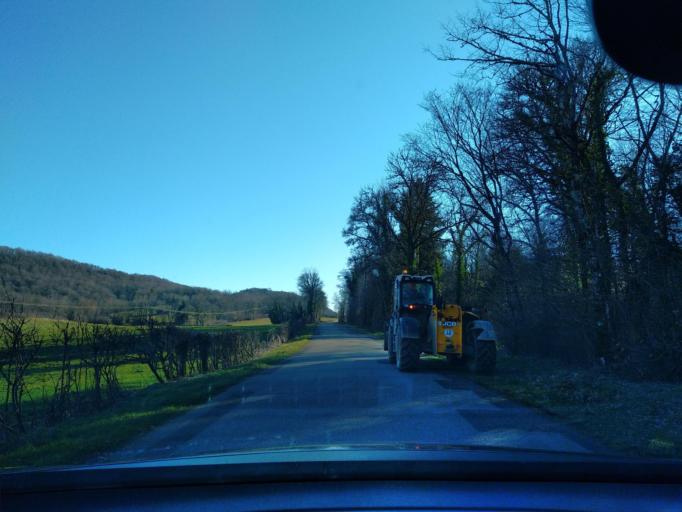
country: FR
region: Franche-Comte
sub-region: Departement du Jura
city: Poligny
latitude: 46.7167
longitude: 5.7392
